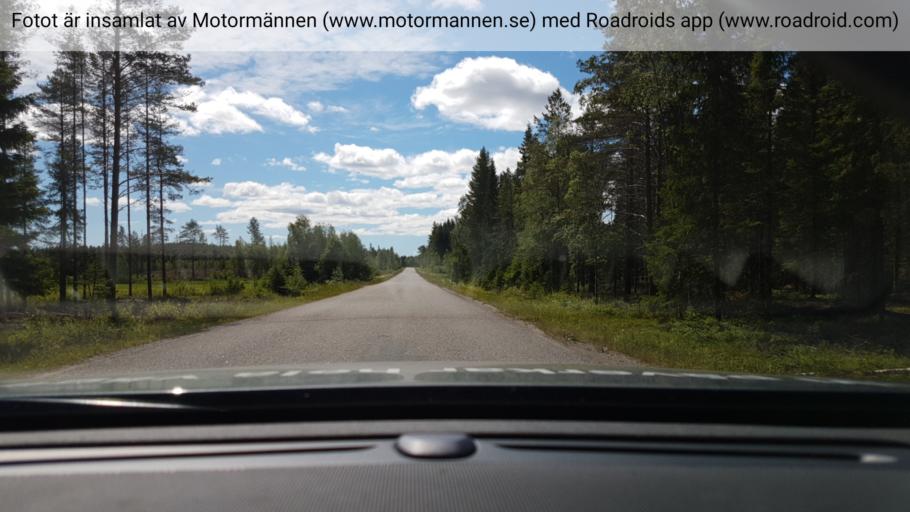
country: SE
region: Vaesterbotten
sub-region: Skelleftea Kommun
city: Burea
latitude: 64.4169
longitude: 21.3516
